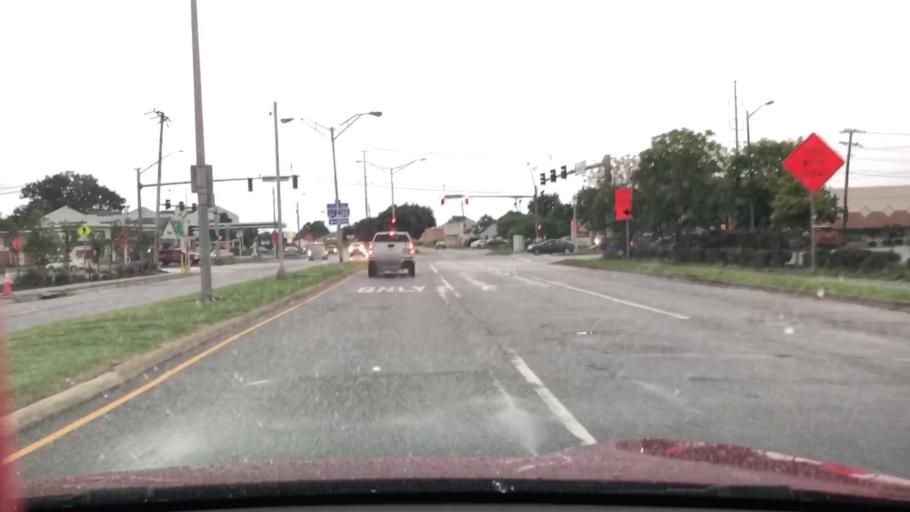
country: US
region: Virginia
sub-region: City of Chesapeake
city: Chesapeake
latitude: 36.8424
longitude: -76.1883
